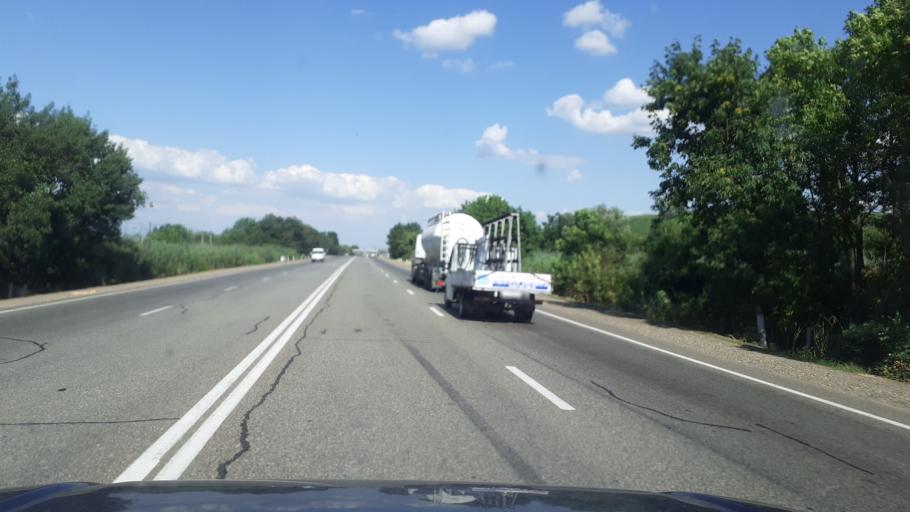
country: RU
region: Krasnodarskiy
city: Afipskiy
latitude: 44.8841
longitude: 38.7952
